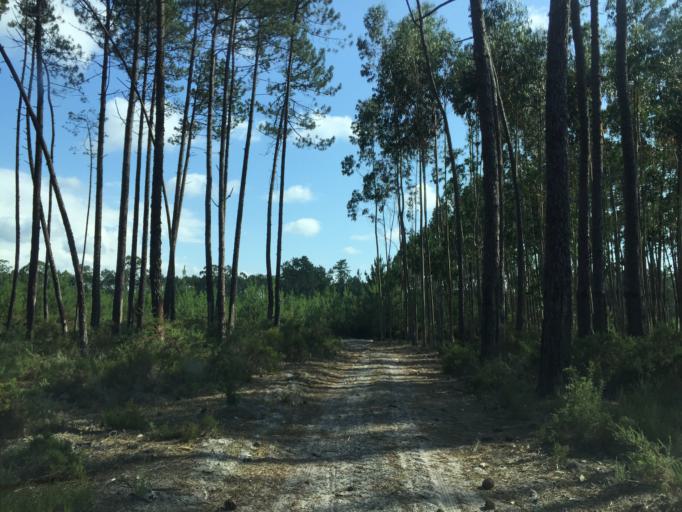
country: PT
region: Leiria
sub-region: Leiria
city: Monte Redondo
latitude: 39.9523
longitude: -8.8238
